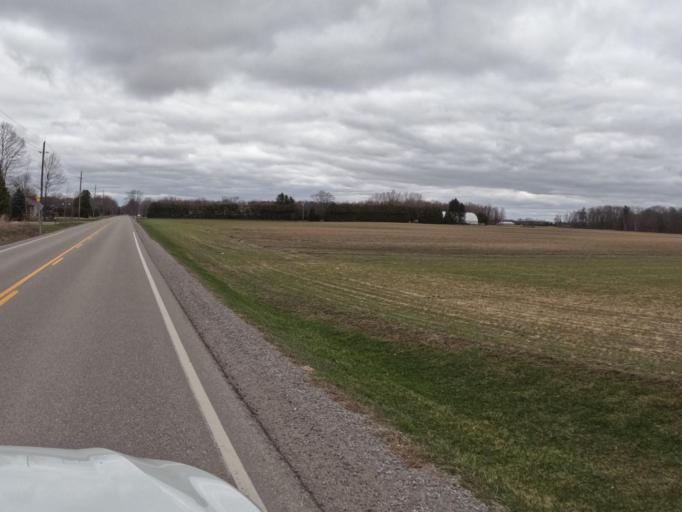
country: CA
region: Ontario
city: Norfolk County
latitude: 42.8684
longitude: -80.4077
